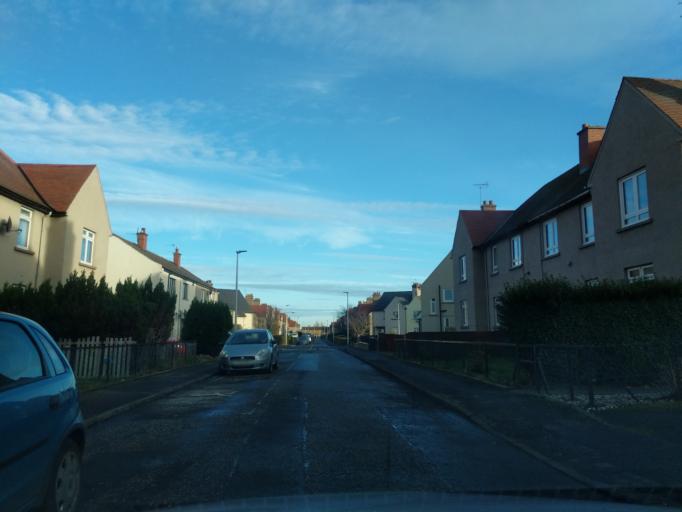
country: GB
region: Scotland
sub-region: Midlothian
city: Loanhead
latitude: 55.8778
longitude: -3.1608
